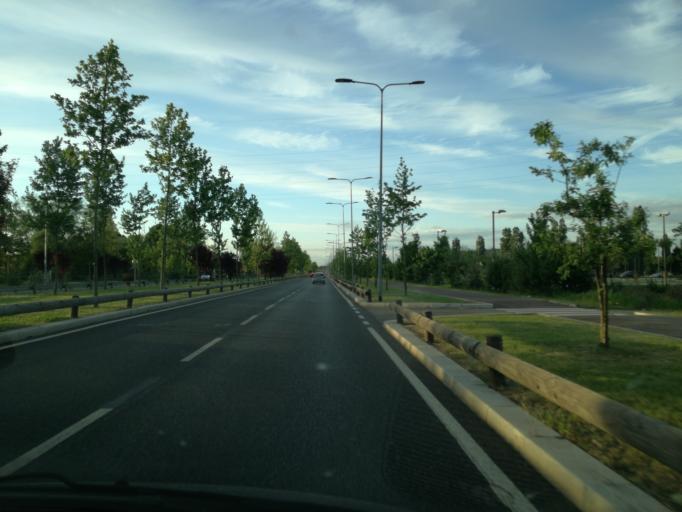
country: IT
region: Lombardy
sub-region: Citta metropolitana di Milano
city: Noverasco-Sporting Mirasole
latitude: 45.4105
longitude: 9.2073
